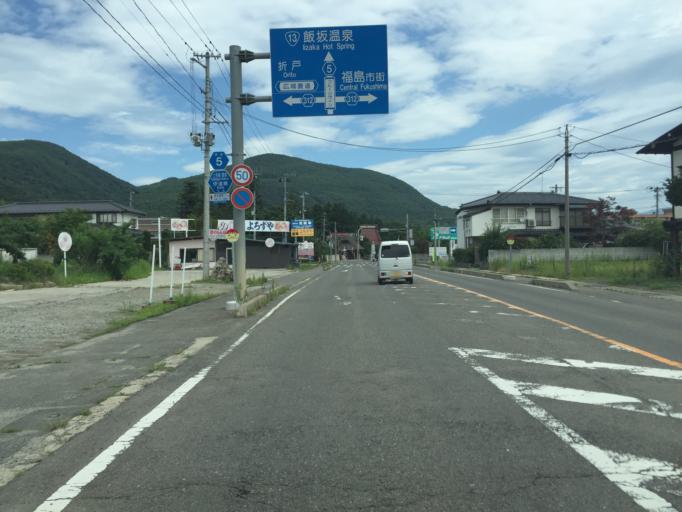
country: JP
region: Fukushima
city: Fukushima-shi
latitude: 37.7974
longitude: 140.4013
